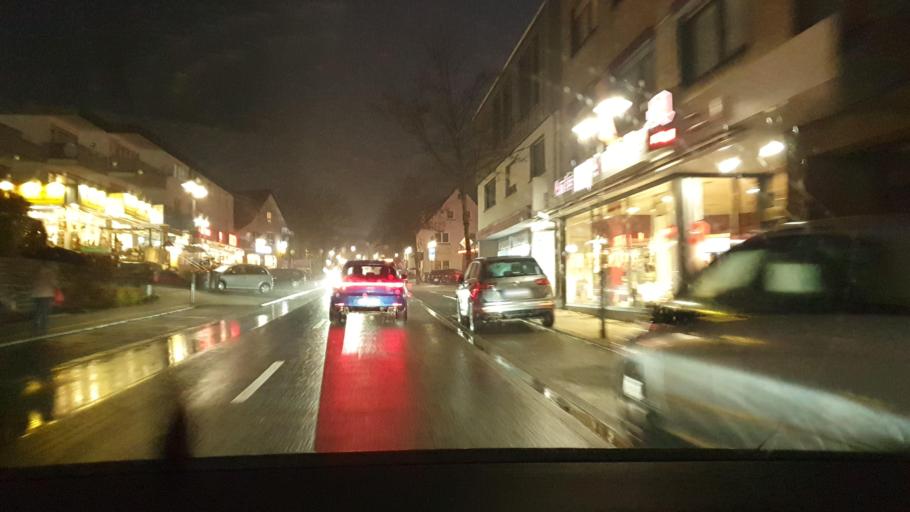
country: DE
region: Rheinland-Pfalz
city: Rennerod
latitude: 50.6076
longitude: 8.0663
